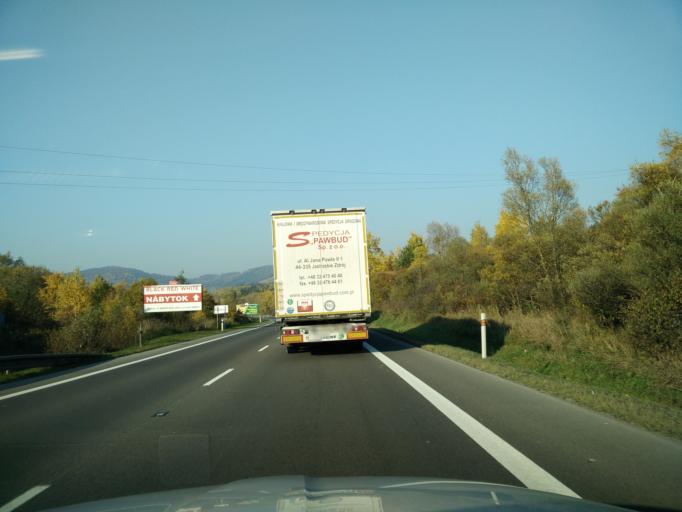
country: SK
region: Zilinsky
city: Cadca
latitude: 49.4044
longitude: 18.8433
